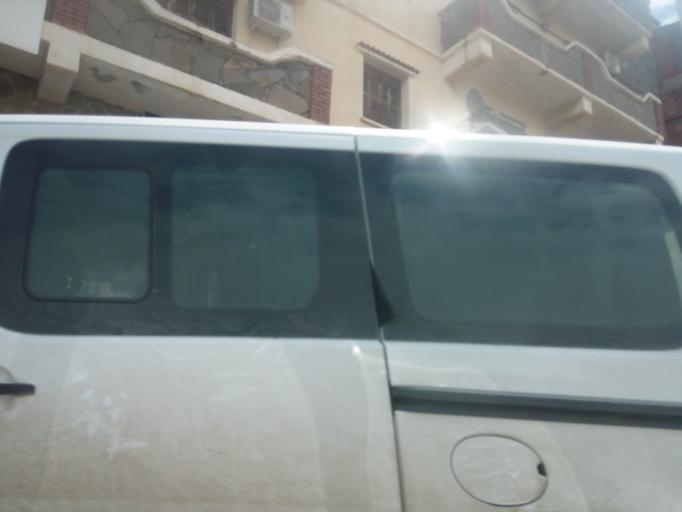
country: DZ
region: Tipaza
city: Douera
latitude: 36.6994
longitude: 2.9675
